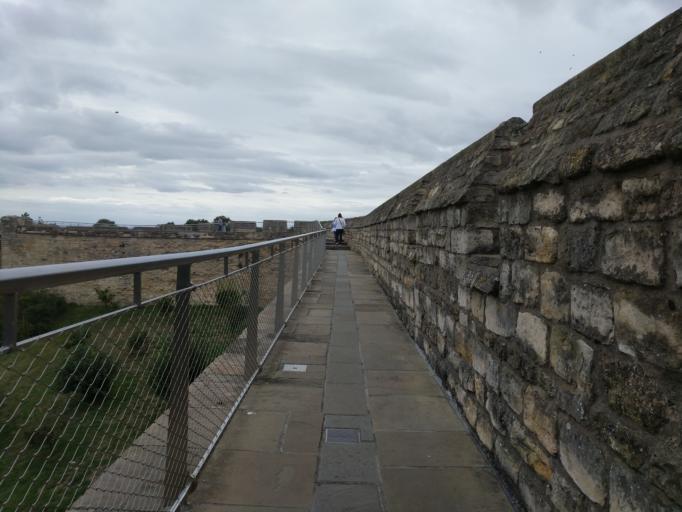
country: GB
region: England
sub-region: Lincolnshire
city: Lincoln
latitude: 53.2357
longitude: -0.5414
